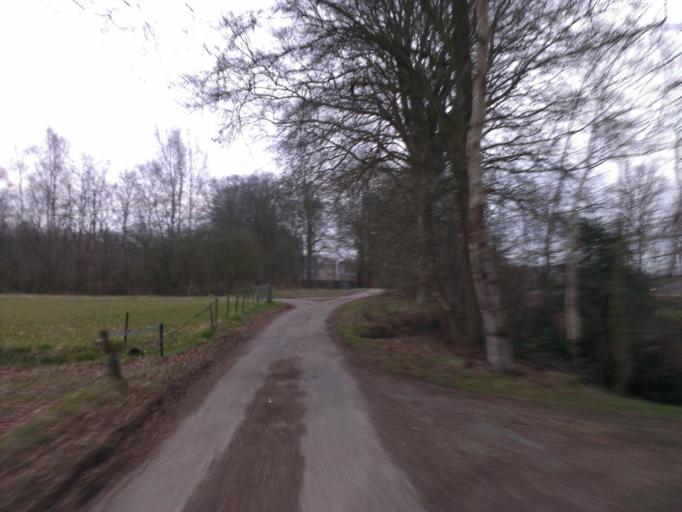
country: NL
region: Gelderland
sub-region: Gemeente Heerde
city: Heerde
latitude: 52.3781
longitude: 6.0168
